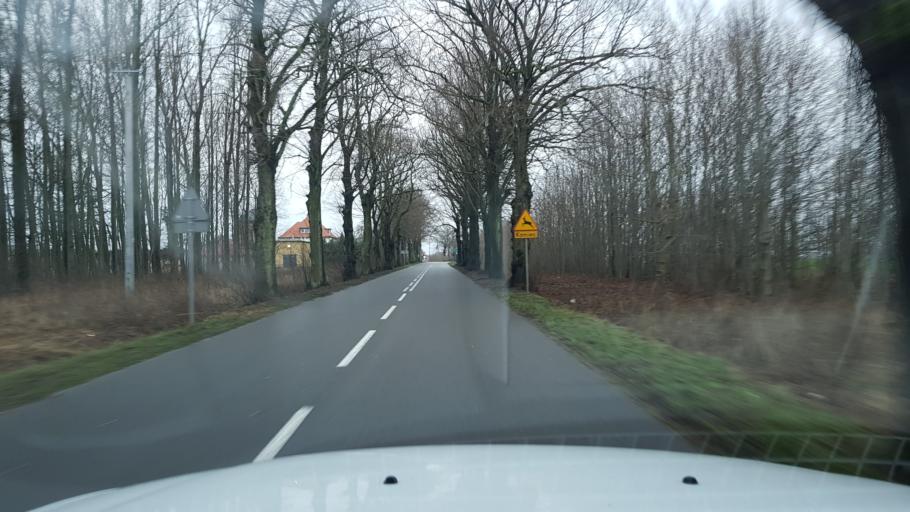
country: PL
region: West Pomeranian Voivodeship
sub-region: Powiat gryficki
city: Trzebiatow
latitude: 54.0607
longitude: 15.3019
